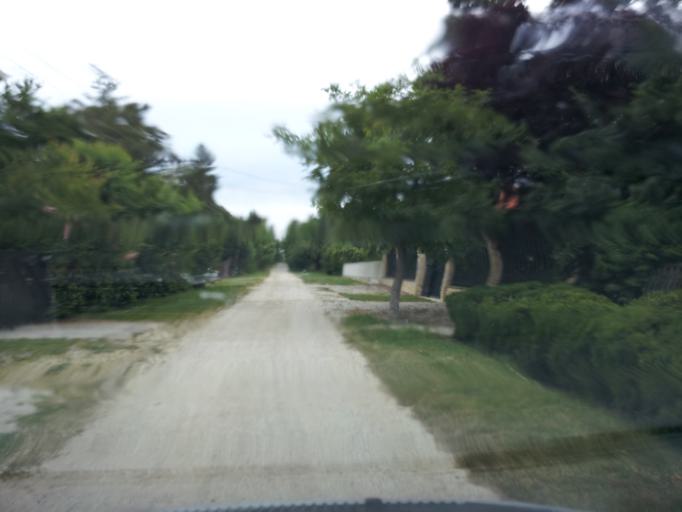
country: HU
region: Veszprem
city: Balatonkenese
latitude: 47.0232
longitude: 18.1548
